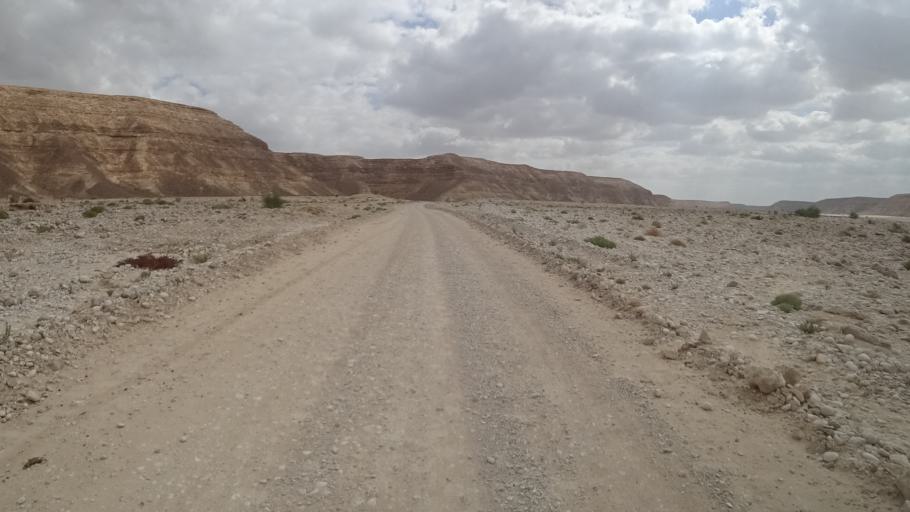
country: YE
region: Al Mahrah
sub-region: Shahan
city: Shihan as Sufla
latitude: 17.4633
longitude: 53.0073
